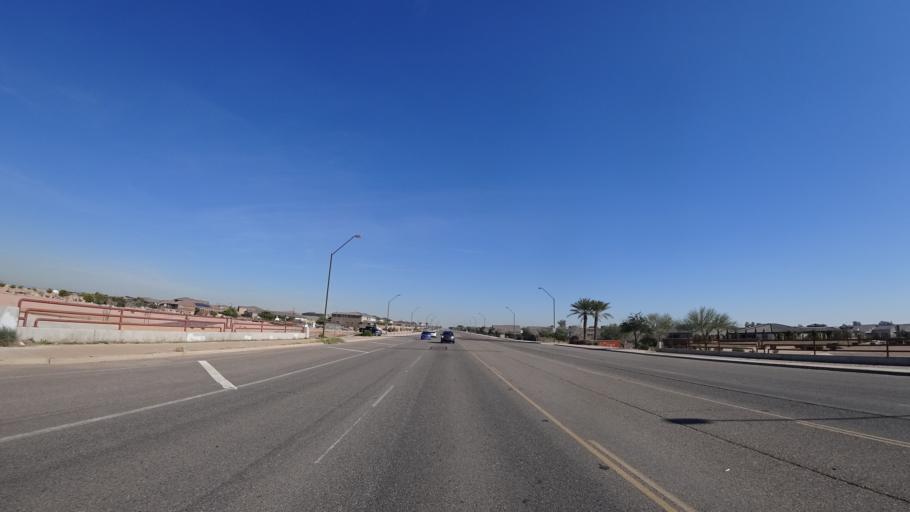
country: US
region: Arizona
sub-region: Maricopa County
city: Litchfield Park
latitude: 33.5082
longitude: -112.3800
